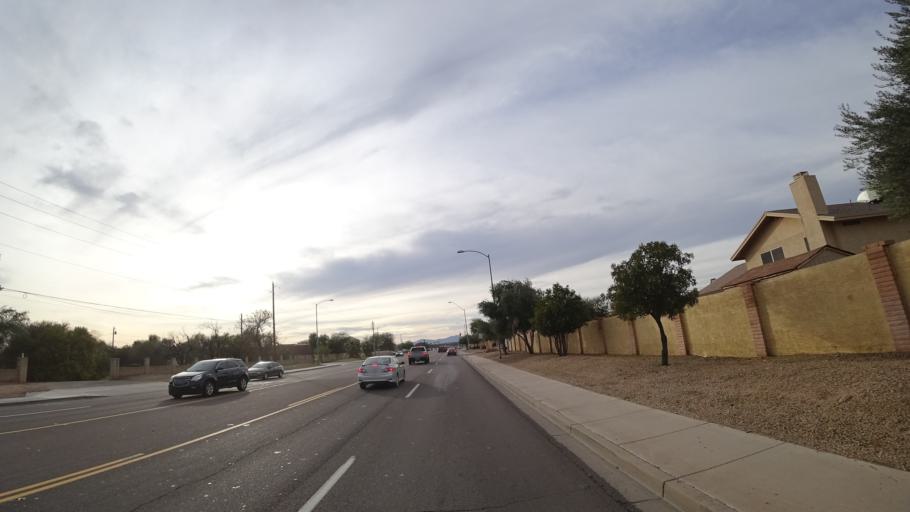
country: US
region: Arizona
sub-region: Maricopa County
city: Peoria
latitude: 33.5664
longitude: -112.2510
